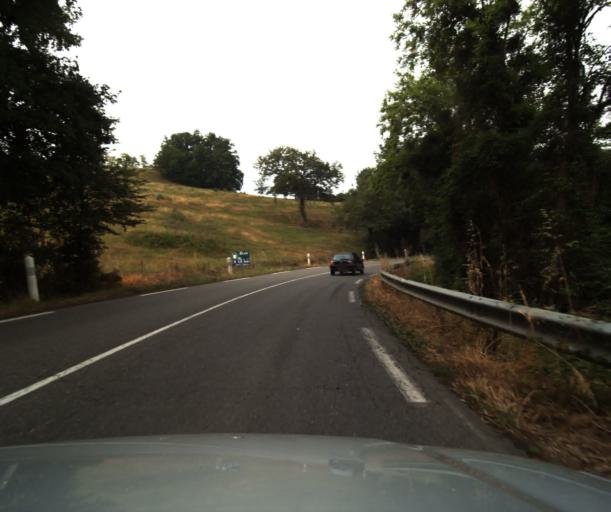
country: FR
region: Midi-Pyrenees
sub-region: Departement du Gers
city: Mielan
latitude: 43.4786
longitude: 0.3371
